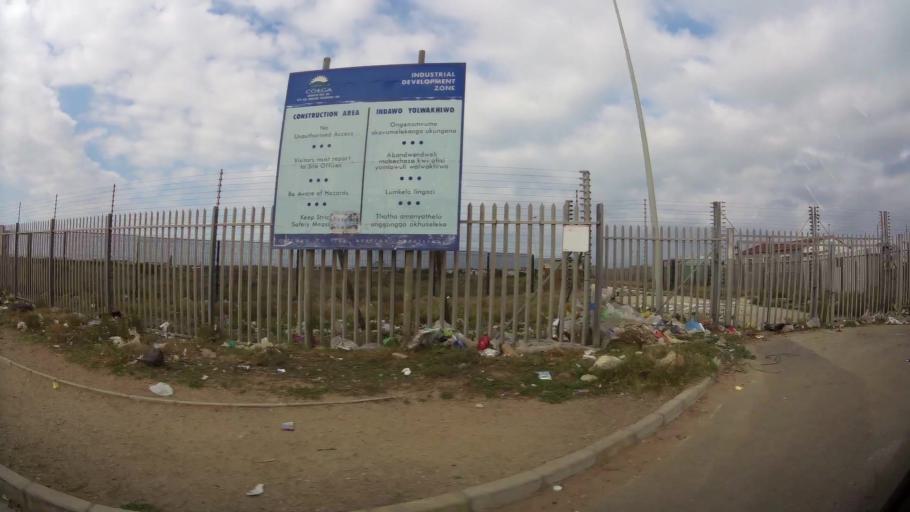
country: ZA
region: Eastern Cape
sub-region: Nelson Mandela Bay Metropolitan Municipality
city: Port Elizabeth
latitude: -33.8224
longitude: 25.6372
